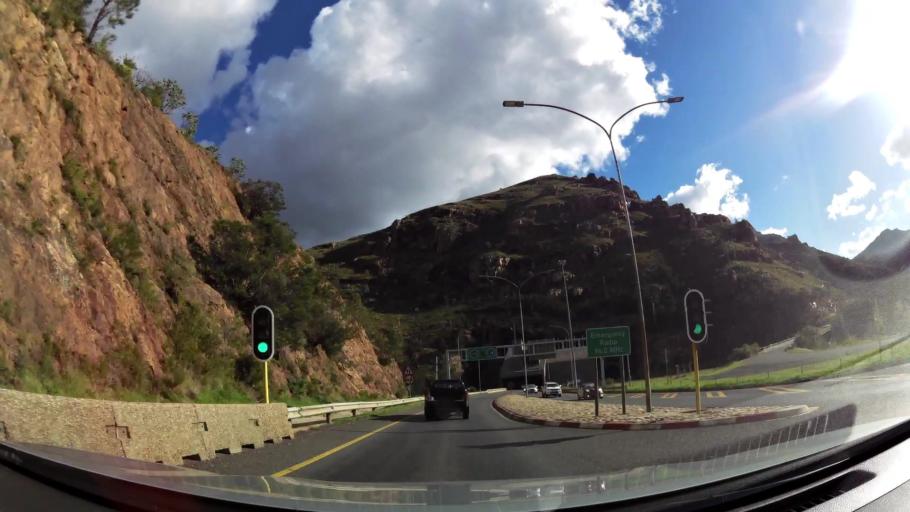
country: ZA
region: Western Cape
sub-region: Cape Winelands District Municipality
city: Paarl
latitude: -33.7326
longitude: 19.1153
